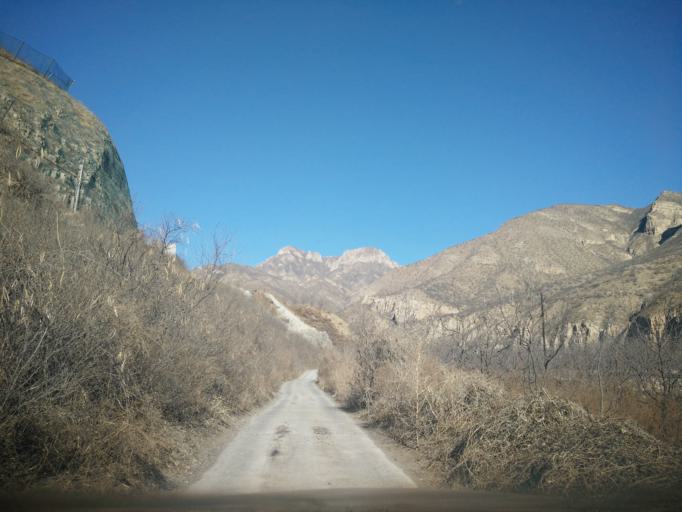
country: CN
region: Beijing
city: Zhaitang
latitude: 40.1635
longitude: 115.6680
